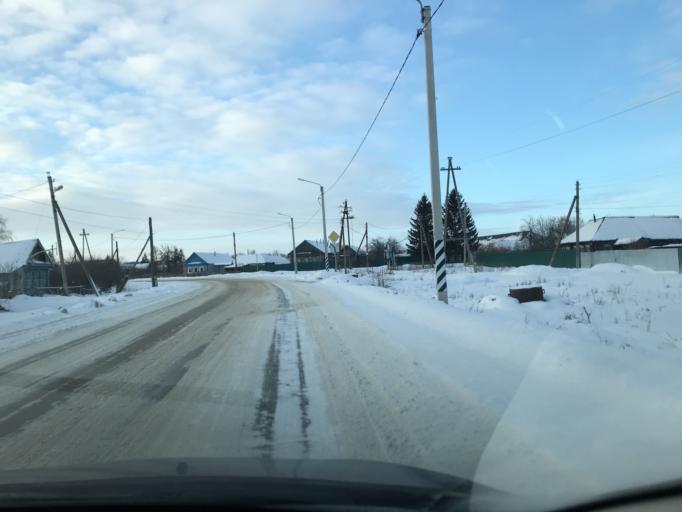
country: RU
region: Ulyanovsk
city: Undory
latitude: 54.6052
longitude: 48.4057
